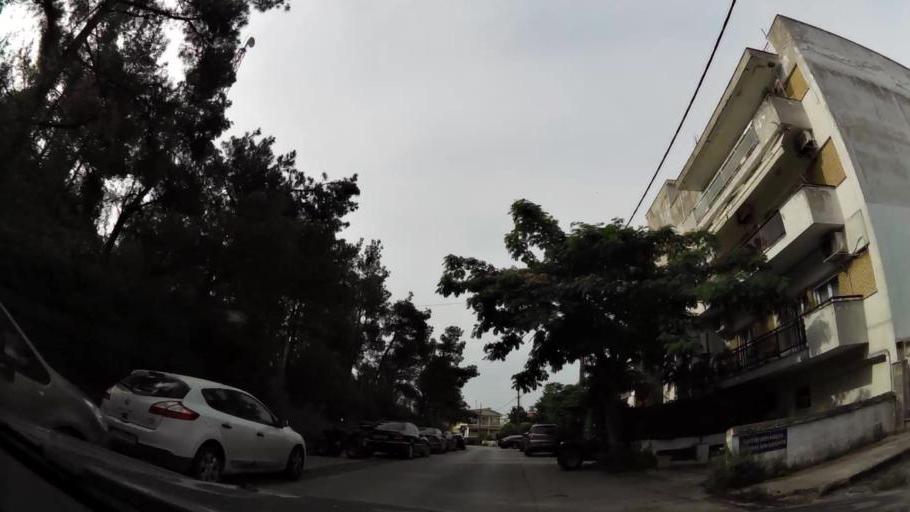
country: GR
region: Central Macedonia
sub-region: Nomos Thessalonikis
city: Panorama
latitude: 40.5881
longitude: 23.0300
